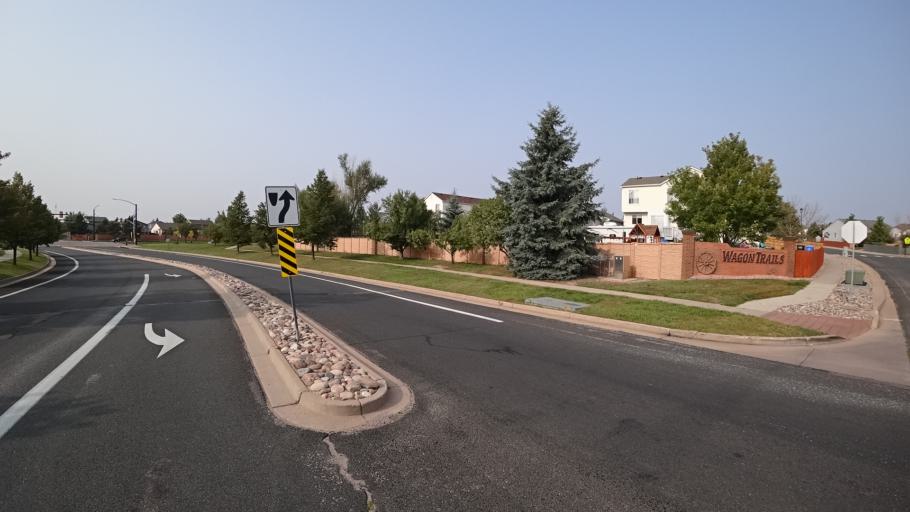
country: US
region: Colorado
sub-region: El Paso County
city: Cimarron Hills
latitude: 38.9306
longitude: -104.7279
